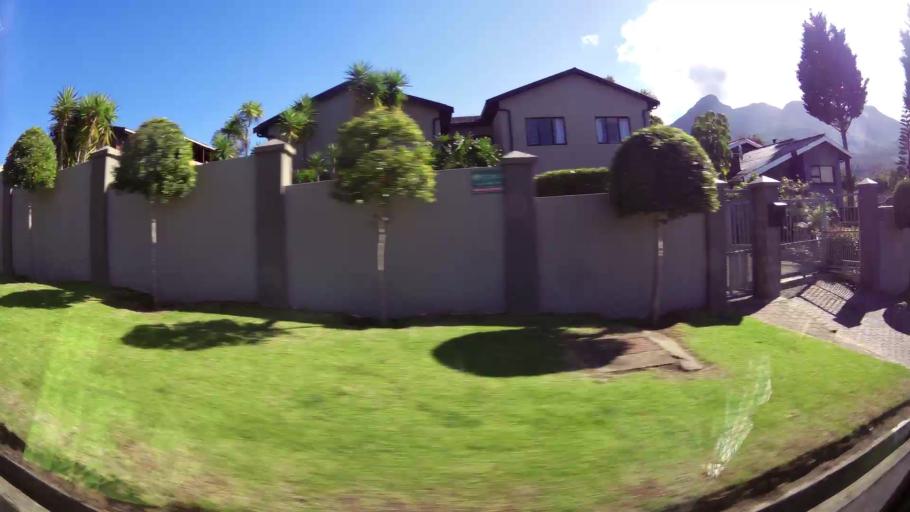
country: ZA
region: Western Cape
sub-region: Eden District Municipality
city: George
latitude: -33.9470
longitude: 22.4764
